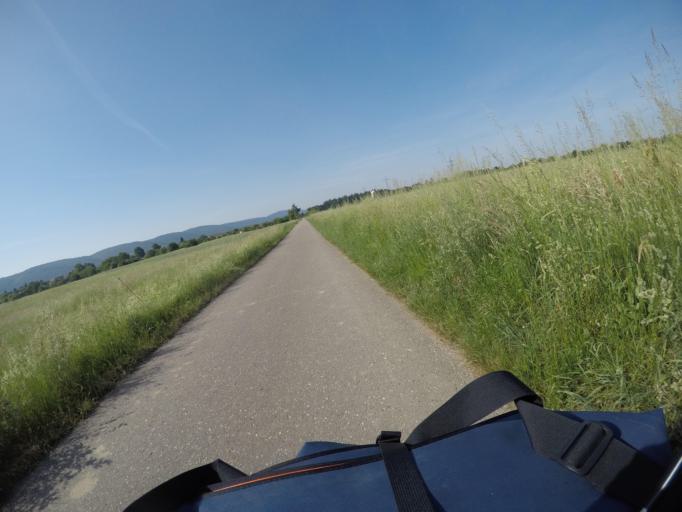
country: DE
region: Baden-Wuerttemberg
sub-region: Karlsruhe Region
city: Ettlingen
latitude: 48.9350
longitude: 8.3644
